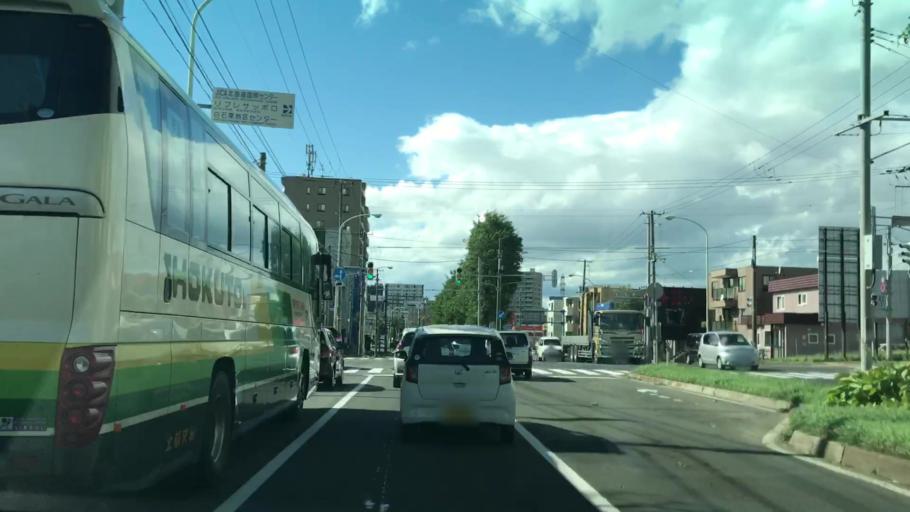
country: JP
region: Hokkaido
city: Sapporo
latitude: 43.0321
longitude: 141.4304
